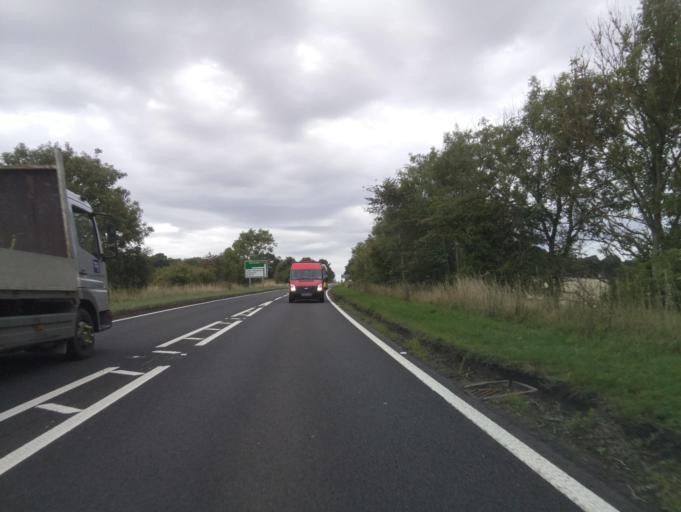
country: GB
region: Scotland
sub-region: Fife
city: High Valleyfield
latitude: 56.0642
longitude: -3.6087
